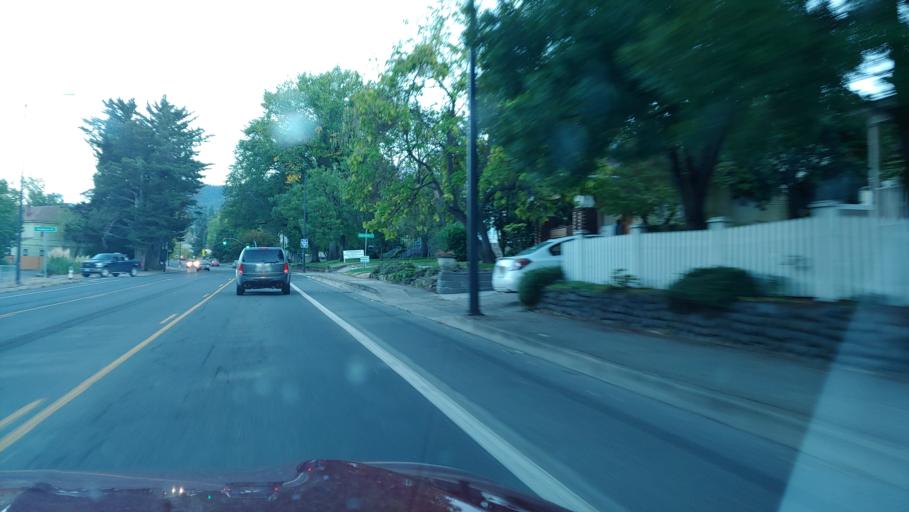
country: US
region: Oregon
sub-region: Jackson County
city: Ashland
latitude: 42.2026
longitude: -122.7192
